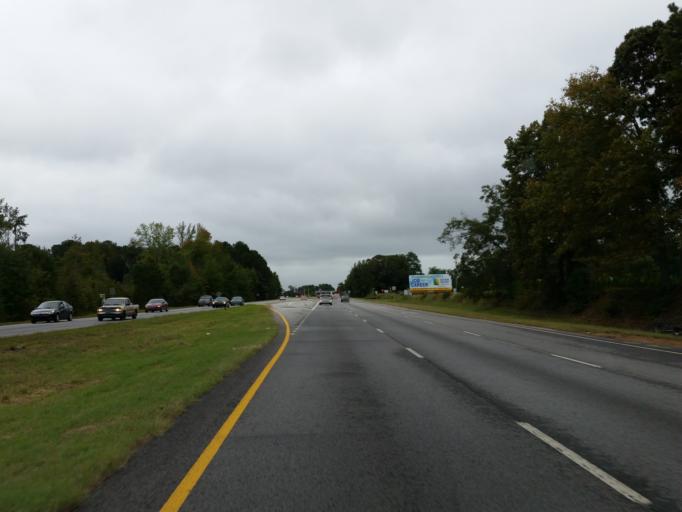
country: US
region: Georgia
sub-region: Henry County
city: Hampton
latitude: 33.3557
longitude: -84.2963
